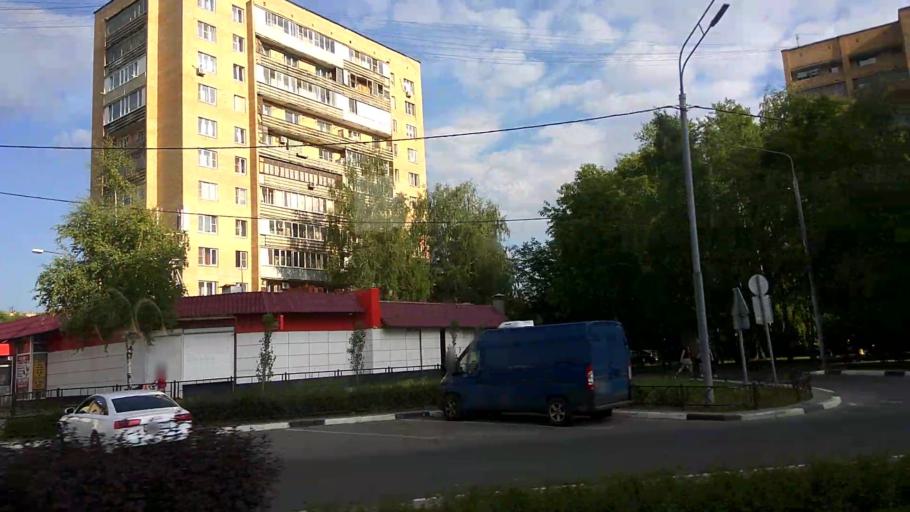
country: RU
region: Moskovskaya
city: Mytishchi
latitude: 55.9150
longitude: 37.7209
